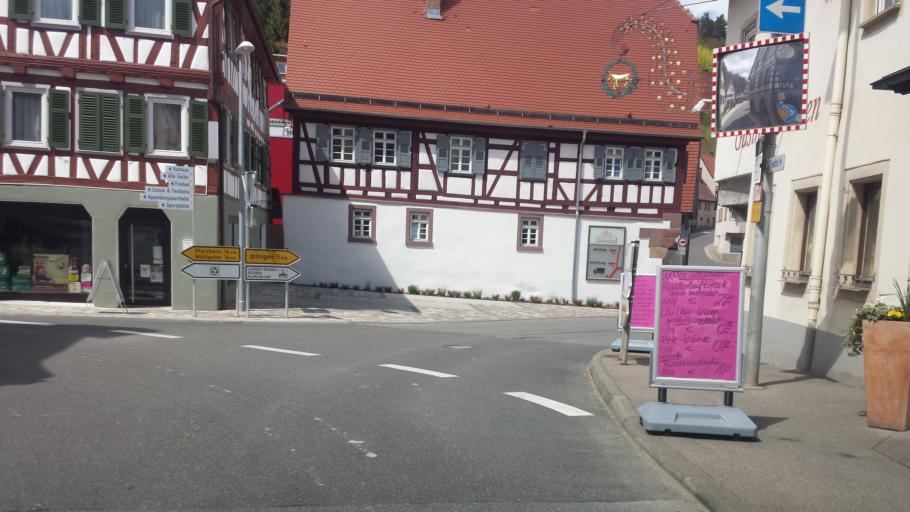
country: DE
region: Baden-Wuerttemberg
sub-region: Karlsruhe Region
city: Monsheim
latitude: 48.8637
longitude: 8.8639
